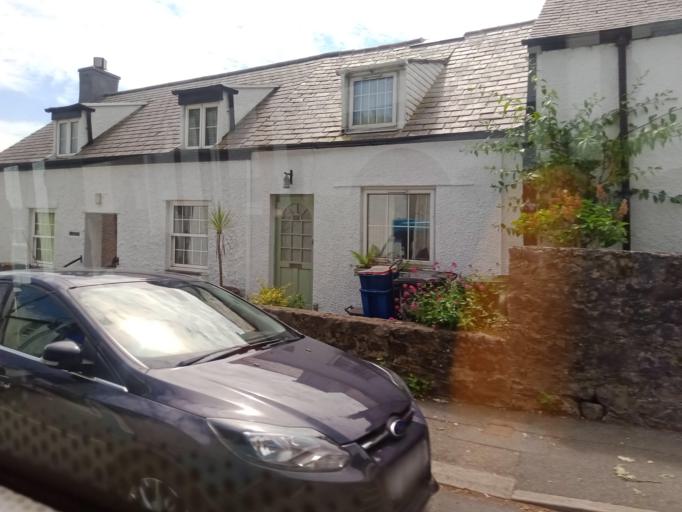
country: GB
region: Wales
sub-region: Anglesey
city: Beaumaris
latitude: 53.2650
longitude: -4.0980
